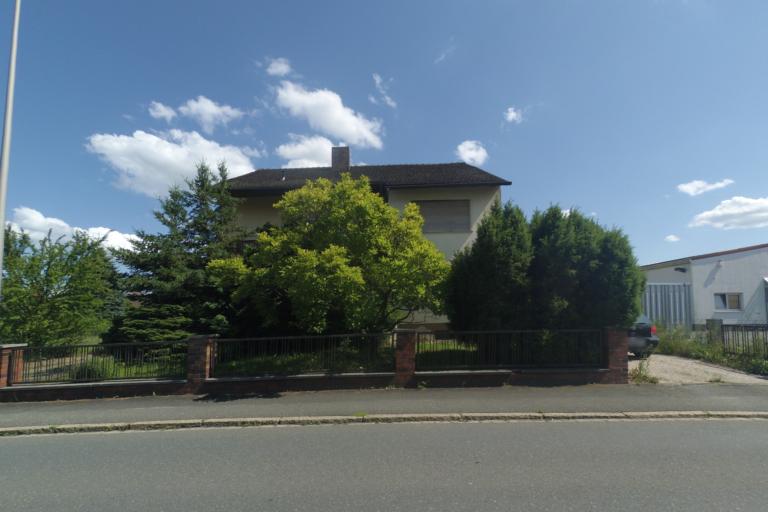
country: DE
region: Bavaria
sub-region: Regierungsbezirk Mittelfranken
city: Adelsdorf
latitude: 49.7138
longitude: 10.8900
